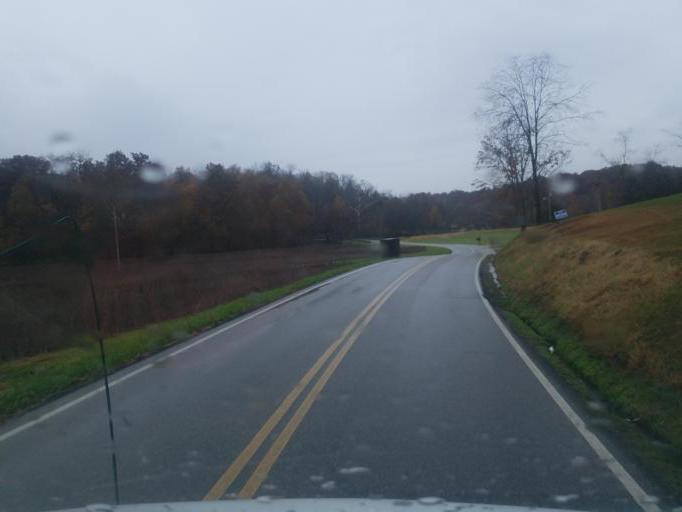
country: US
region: West Virginia
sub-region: Wood County
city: Blennerhassett
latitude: 39.3344
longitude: -81.6219
